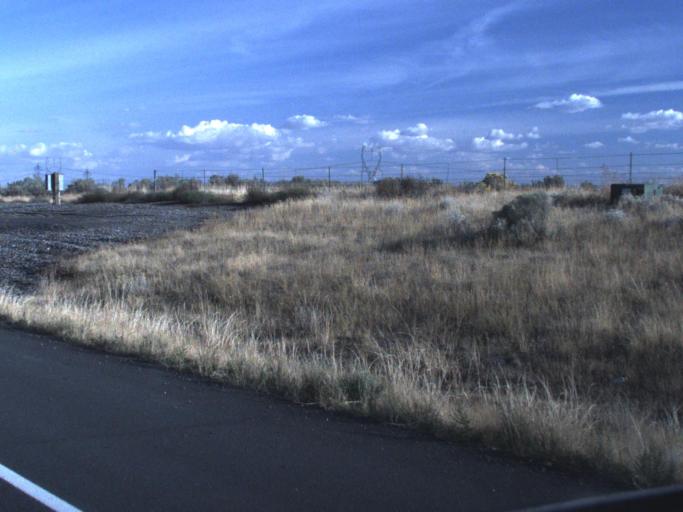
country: US
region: Oregon
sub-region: Umatilla County
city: Umatilla
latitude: 45.9443
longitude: -119.3479
